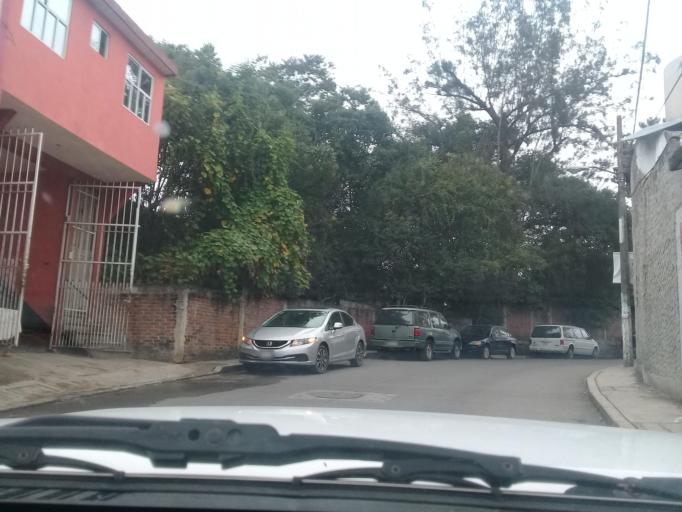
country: MX
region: Veracruz
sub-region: Xalapa
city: Xalapa de Enriquez
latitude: 19.5137
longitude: -96.9123
